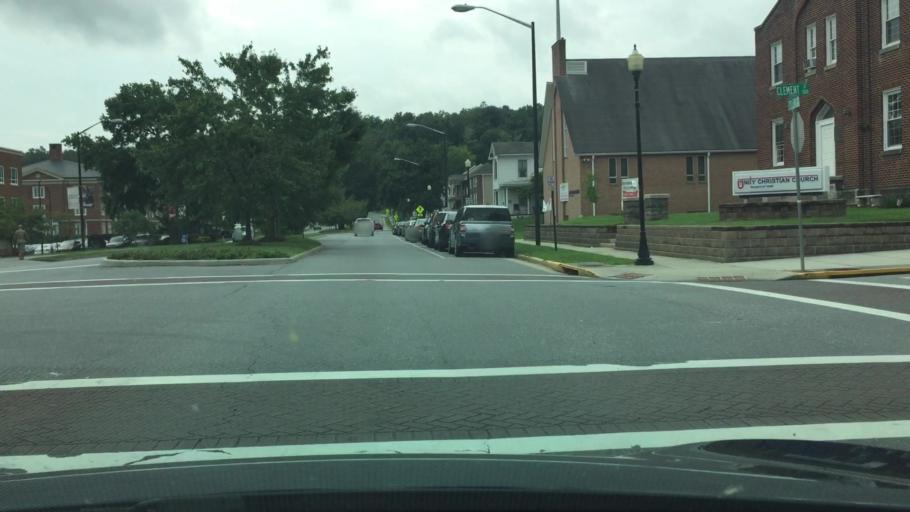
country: US
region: Virginia
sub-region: City of Radford
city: Radford
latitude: 37.1378
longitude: -80.5531
